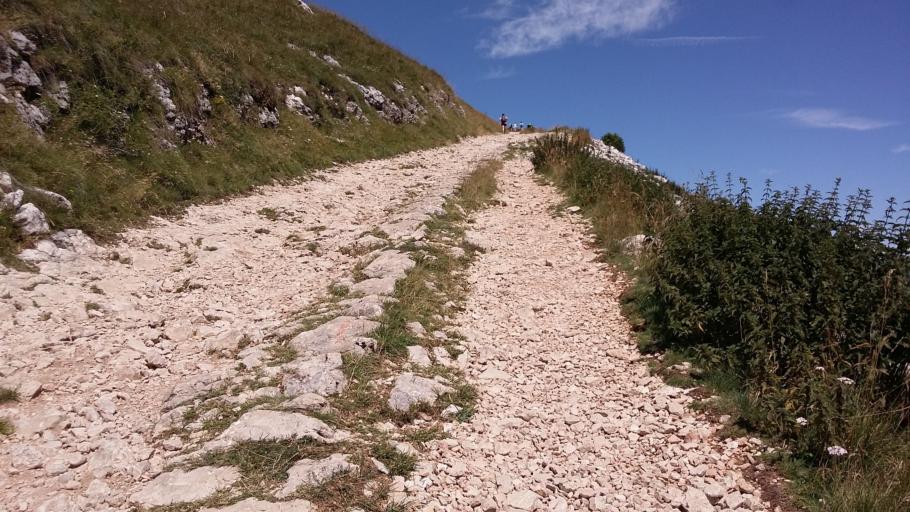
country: IT
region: Trentino-Alto Adige
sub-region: Provincia di Trento
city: Brentonico
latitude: 45.8013
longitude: 10.8950
